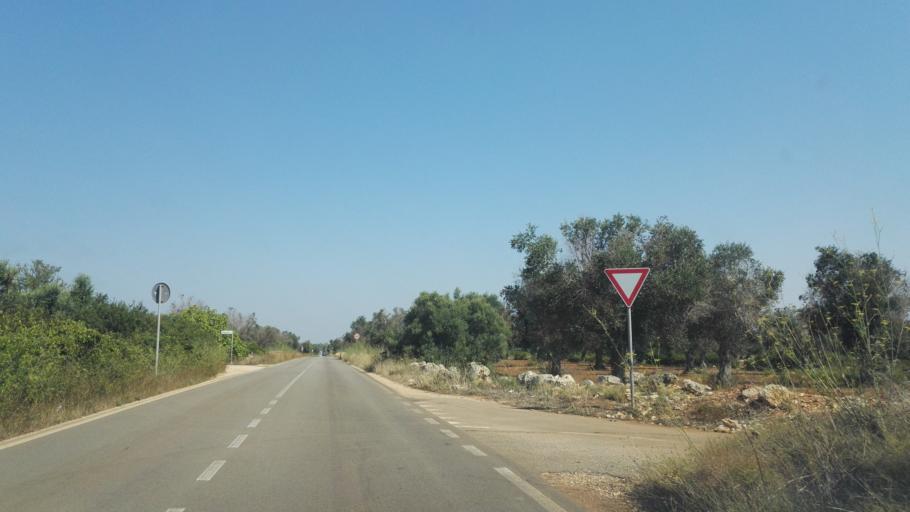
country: IT
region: Apulia
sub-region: Provincia di Lecce
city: Nardo
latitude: 40.1859
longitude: 17.9708
